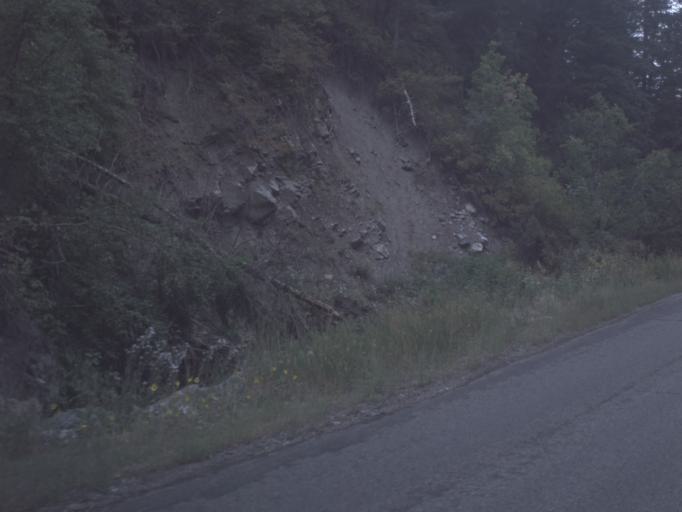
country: US
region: Utah
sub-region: Utah County
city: Orem
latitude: 40.3897
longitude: -111.5749
